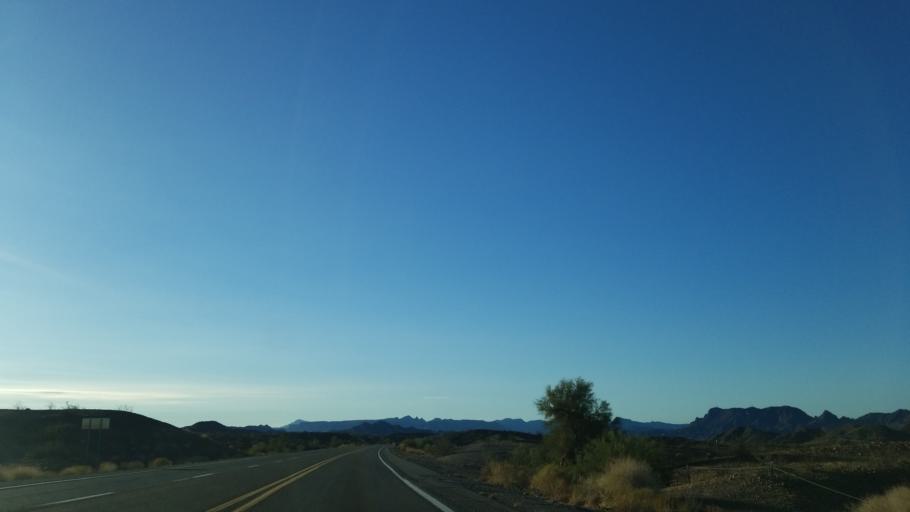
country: US
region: Arizona
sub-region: Mohave County
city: Lake Havasu City
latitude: 34.3907
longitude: -114.1706
